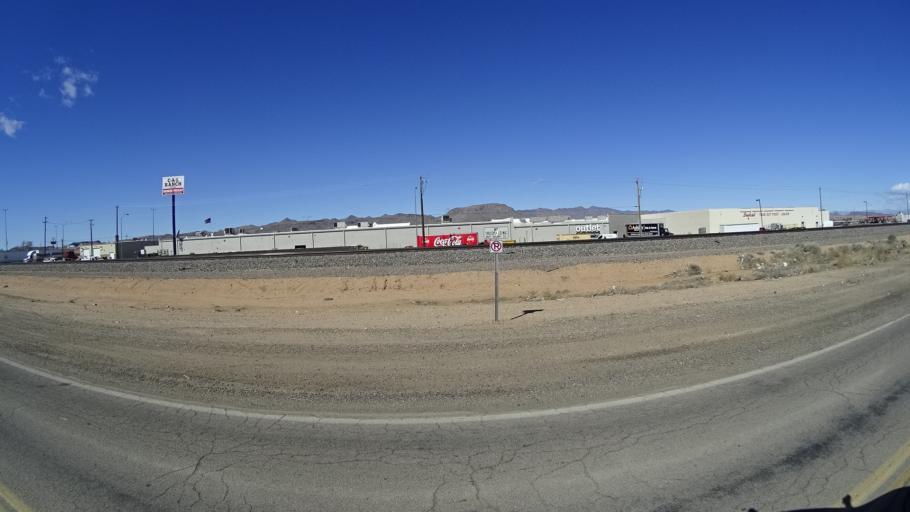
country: US
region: Arizona
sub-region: Mohave County
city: New Kingman-Butler
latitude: 35.2197
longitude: -114.0041
